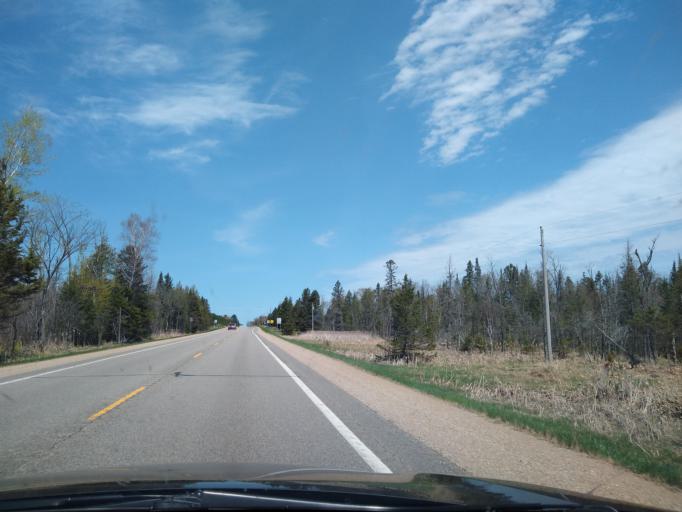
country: US
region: Michigan
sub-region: Delta County
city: Gladstone
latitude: 46.0754
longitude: -86.9810
